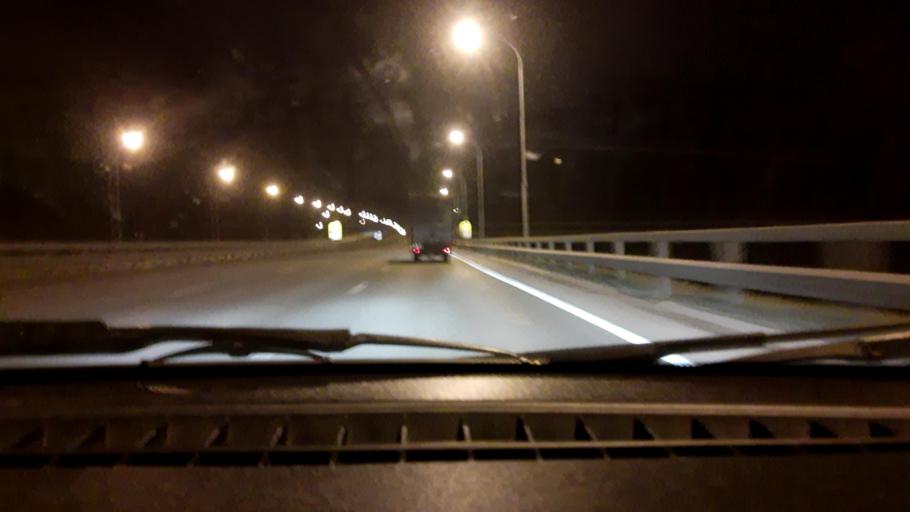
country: RU
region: Bashkortostan
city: Ufa
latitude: 54.6467
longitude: 56.0162
